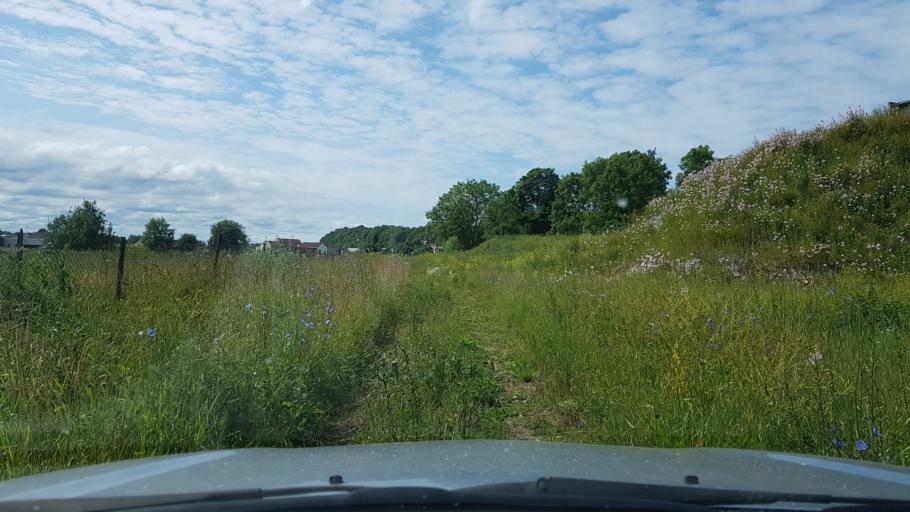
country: EE
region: Ida-Virumaa
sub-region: Sillamaee linn
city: Sillamae
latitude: 59.3716
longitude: 27.8760
